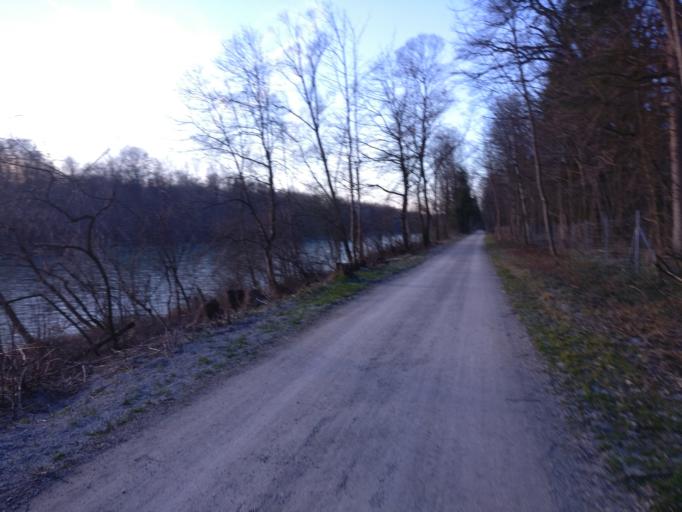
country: DE
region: Bavaria
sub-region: Upper Bavaria
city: Freilassing
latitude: 47.8657
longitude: 12.9917
